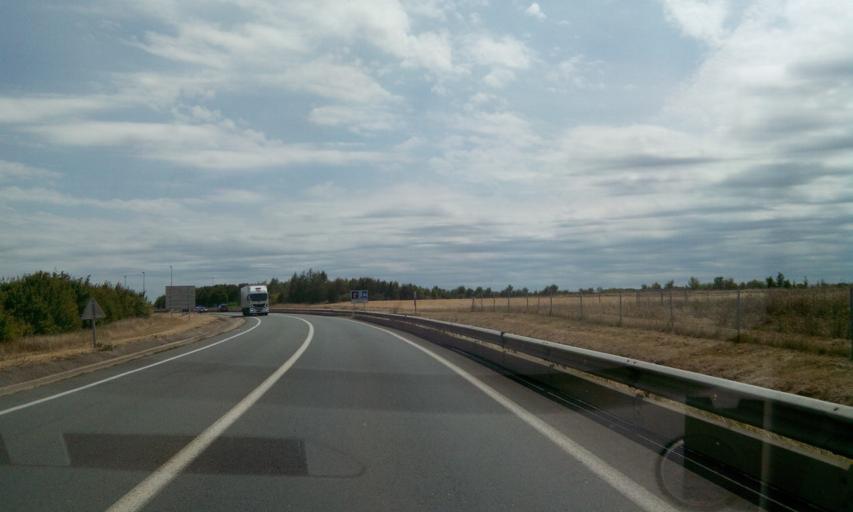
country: FR
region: Poitou-Charentes
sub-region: Departement des Deux-Sevres
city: Vouille
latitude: 46.3092
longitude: -0.3711
